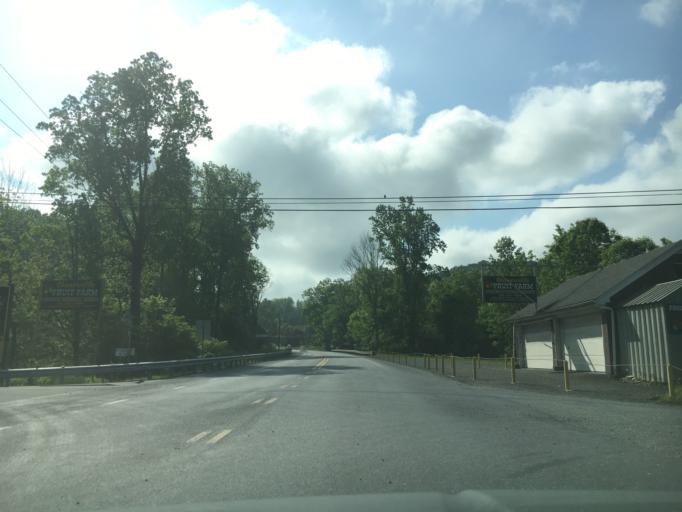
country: US
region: Pennsylvania
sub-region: Berks County
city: New Berlinville
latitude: 40.3677
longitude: -75.7072
